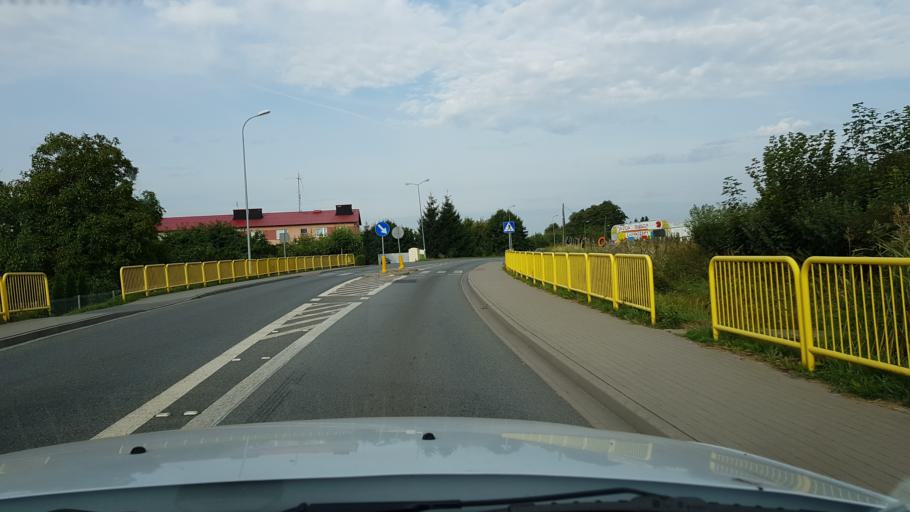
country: PL
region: West Pomeranian Voivodeship
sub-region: Powiat slawienski
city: Slawno
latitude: 54.3706
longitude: 16.6553
